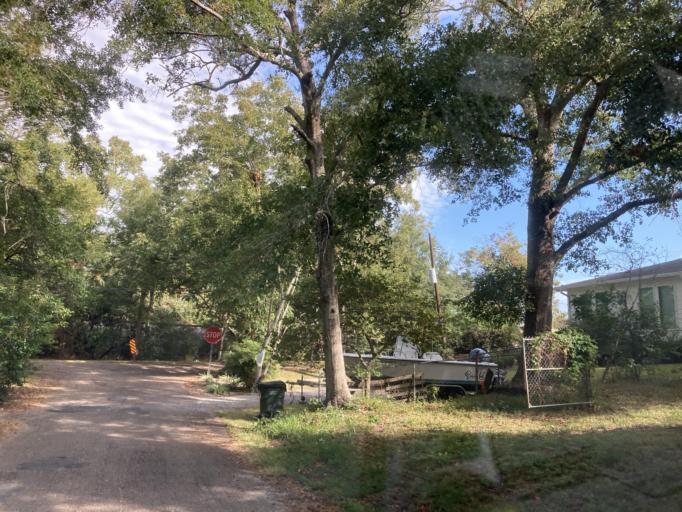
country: US
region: Mississippi
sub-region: Jackson County
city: Ocean Springs
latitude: 30.4146
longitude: -88.8310
